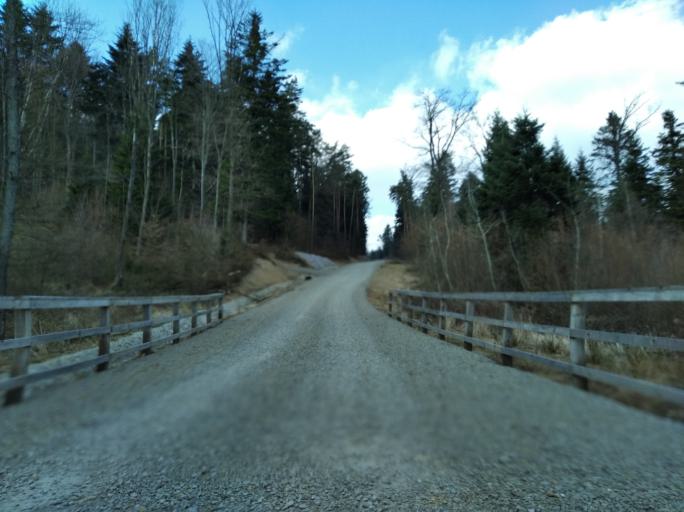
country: PL
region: Subcarpathian Voivodeship
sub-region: Powiat strzyzowski
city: Strzyzow
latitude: 49.8153
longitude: 21.8154
